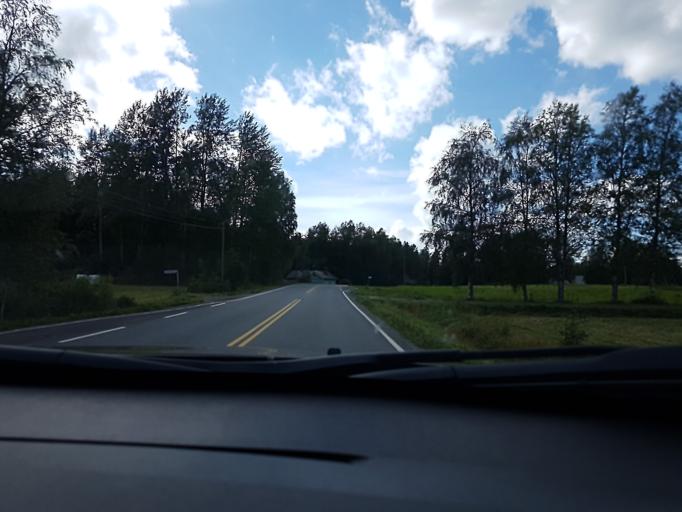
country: FI
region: Southern Ostrobothnia
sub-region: Jaerviseutu
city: Soini
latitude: 62.8527
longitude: 24.2493
